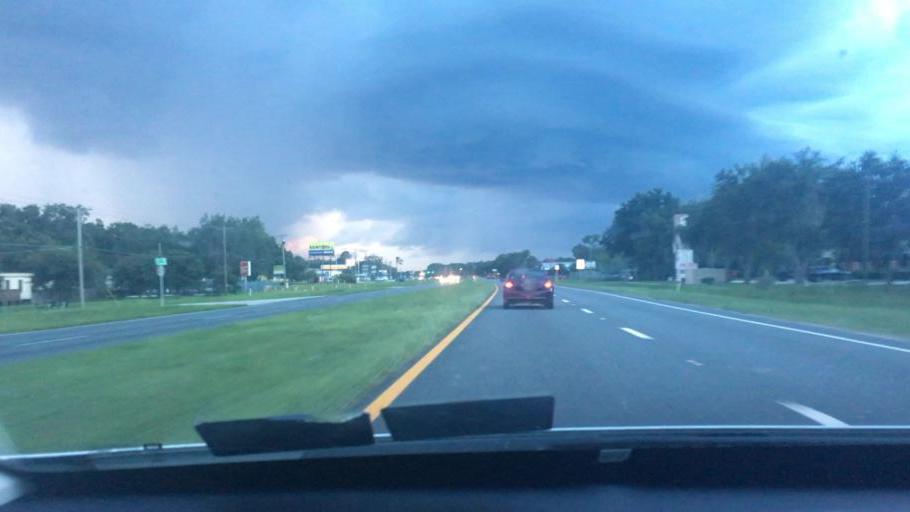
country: US
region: Florida
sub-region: Orange County
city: Bithlo
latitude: 28.5507
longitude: -81.0987
